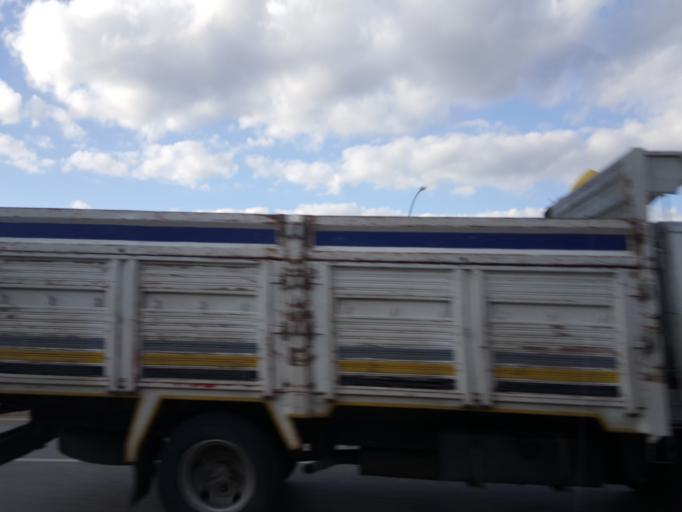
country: TR
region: Tokat
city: Tokat
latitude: 40.3350
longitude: 36.4837
